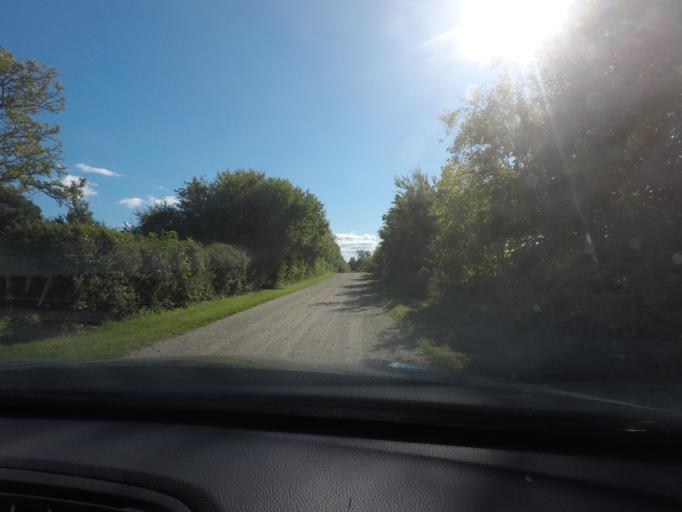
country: DK
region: Zealand
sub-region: Guldborgsund Kommune
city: Sakskobing
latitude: 54.9712
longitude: 11.5584
